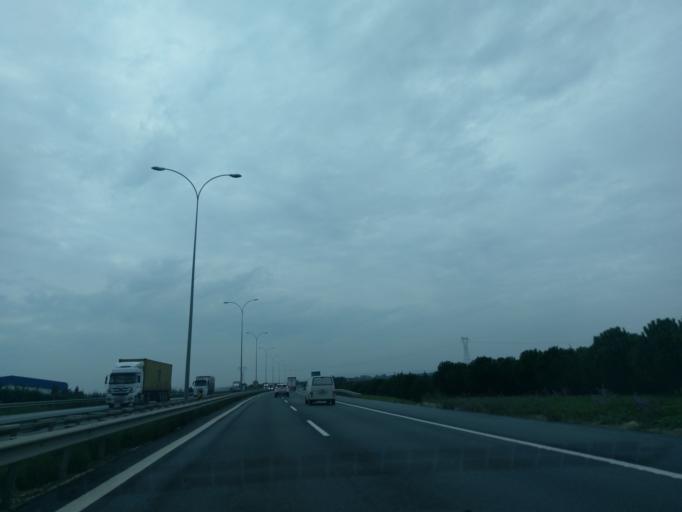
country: TR
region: Istanbul
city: Silivri
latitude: 41.1186
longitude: 28.2103
